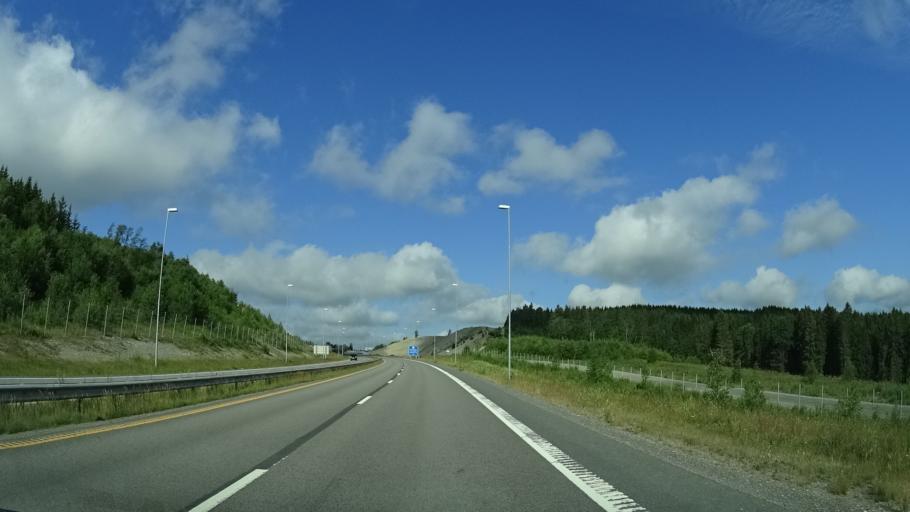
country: NO
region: Ostfold
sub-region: Eidsberg
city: Mysen
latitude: 59.5770
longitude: 11.2969
